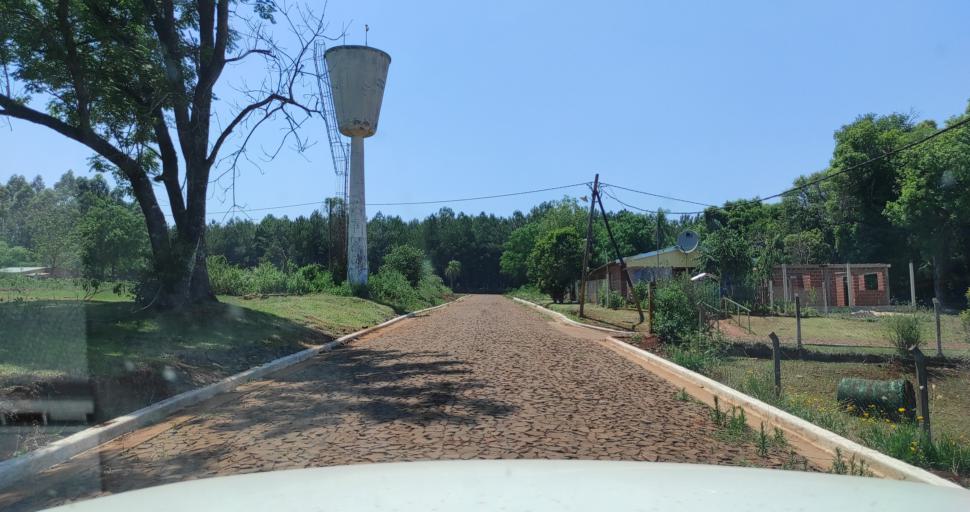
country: AR
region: Misiones
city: Santo Pipo
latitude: -27.1087
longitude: -55.3435
